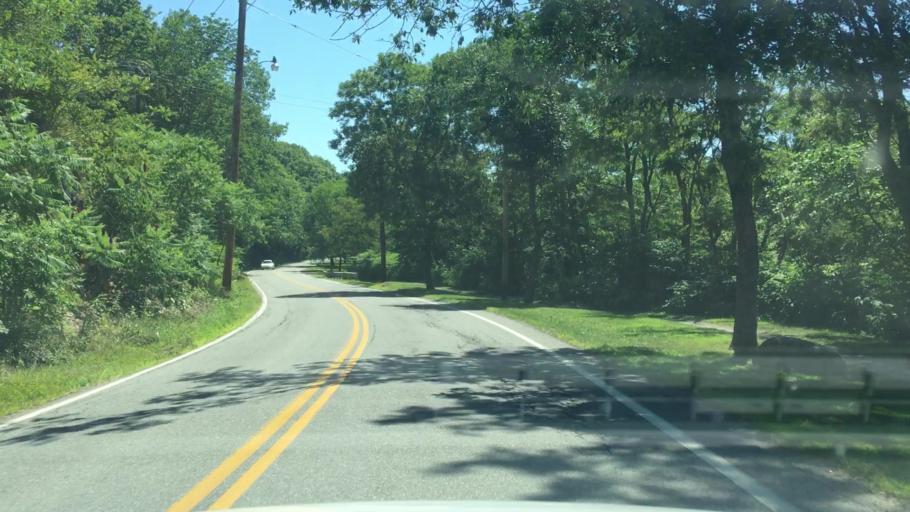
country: US
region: Maine
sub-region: Penobscot County
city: Bangor
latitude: 44.8146
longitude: -68.7873
